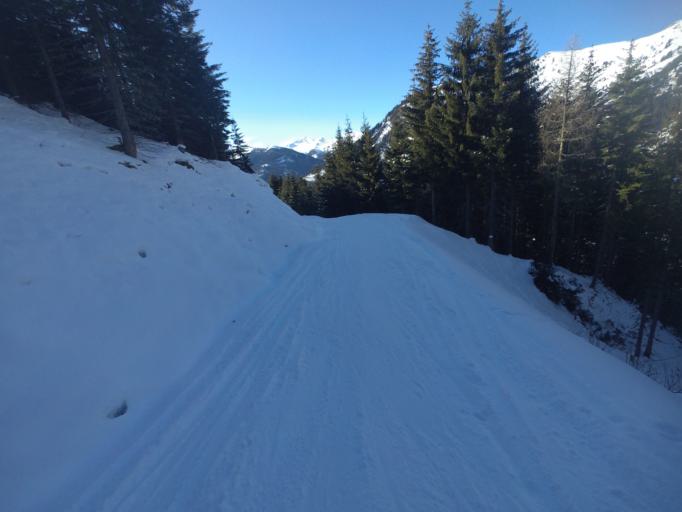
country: AT
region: Salzburg
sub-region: Politischer Bezirk Sankt Johann im Pongau
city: Huttschlag
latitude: 47.1839
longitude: 13.2801
